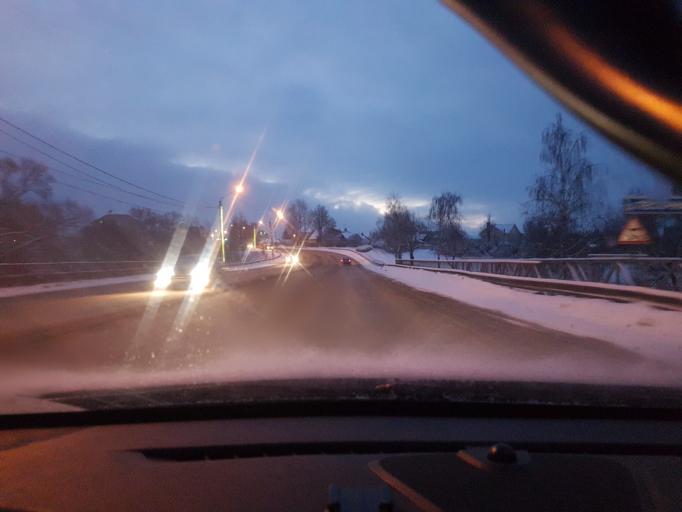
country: RU
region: Moskovskaya
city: Istra
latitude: 55.9099
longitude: 36.8749
